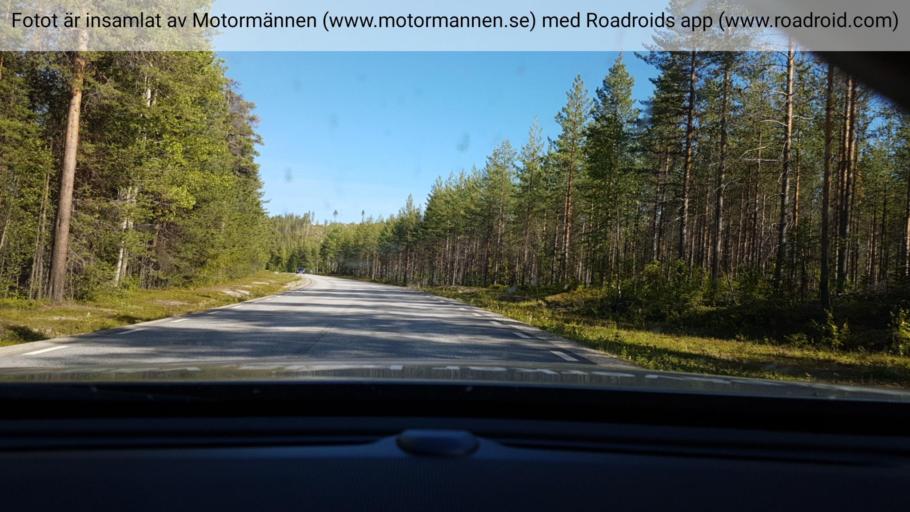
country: SE
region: Vaesterbotten
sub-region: Lycksele Kommun
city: Lycksele
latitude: 64.6295
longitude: 18.5791
